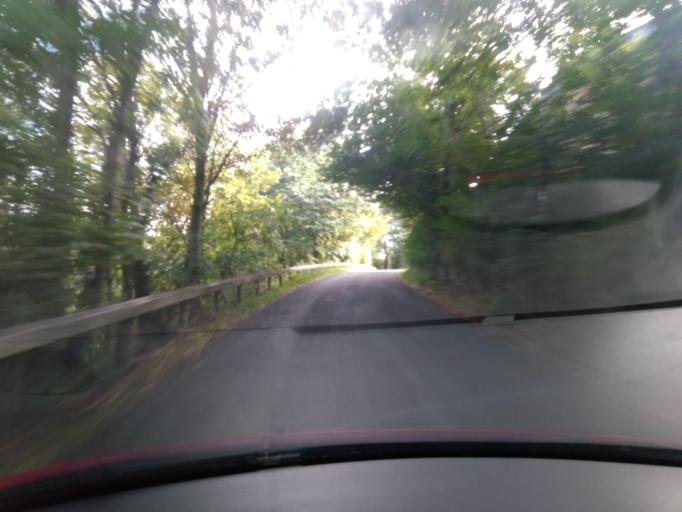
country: GB
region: Scotland
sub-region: The Scottish Borders
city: Kelso
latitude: 55.5024
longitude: -2.3485
